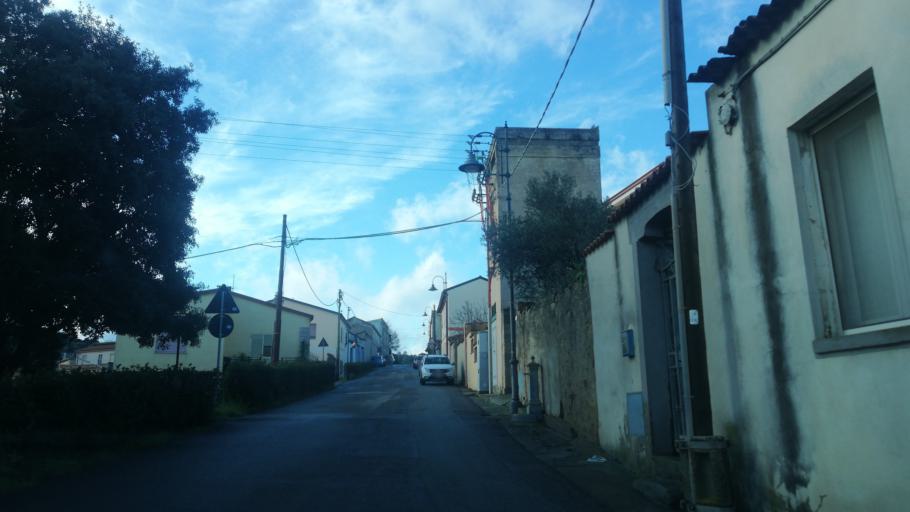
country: IT
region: Sardinia
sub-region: Provincia di Medio Campidano
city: Villanovaforru
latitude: 39.6327
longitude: 8.8664
